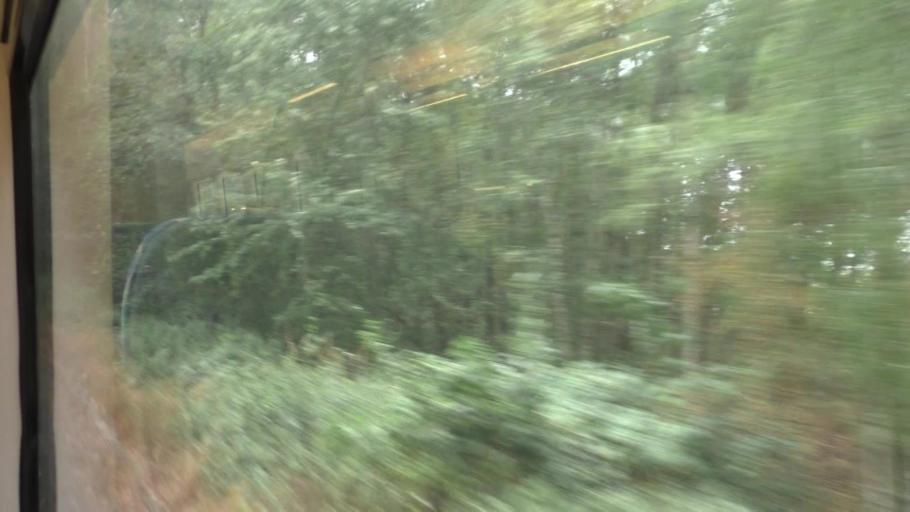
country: DE
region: Saxony
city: Goerlitz
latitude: 51.1176
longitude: 14.9673
